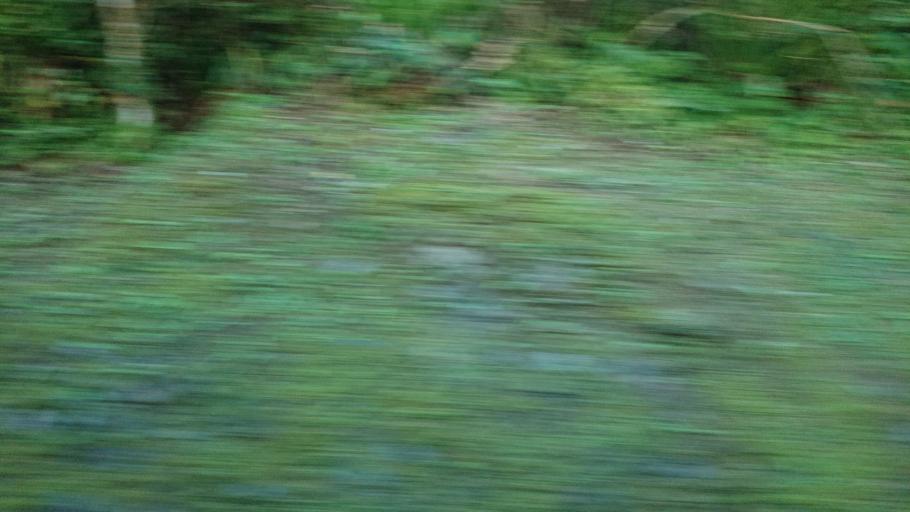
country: TW
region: Taiwan
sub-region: Yilan
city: Yilan
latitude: 24.5780
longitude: 121.4824
